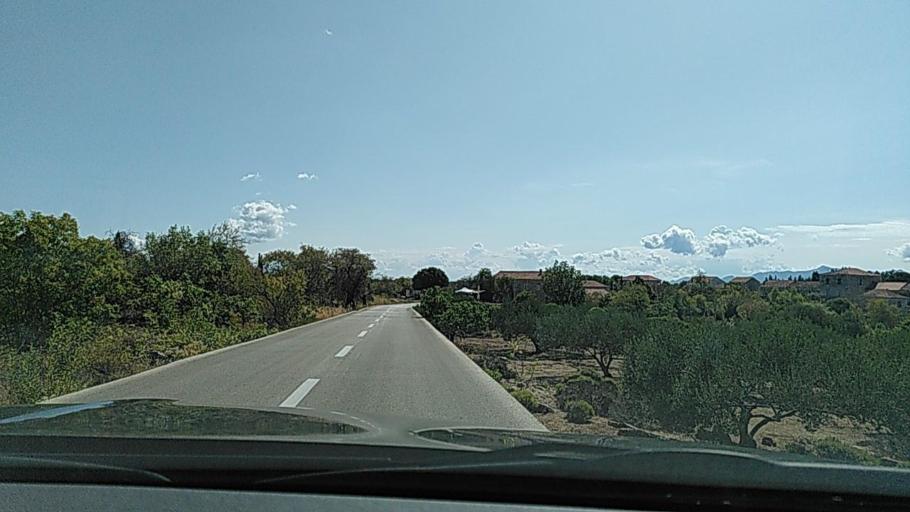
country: HR
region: Splitsko-Dalmatinska
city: Tucepi
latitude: 43.1311
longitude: 16.9818
